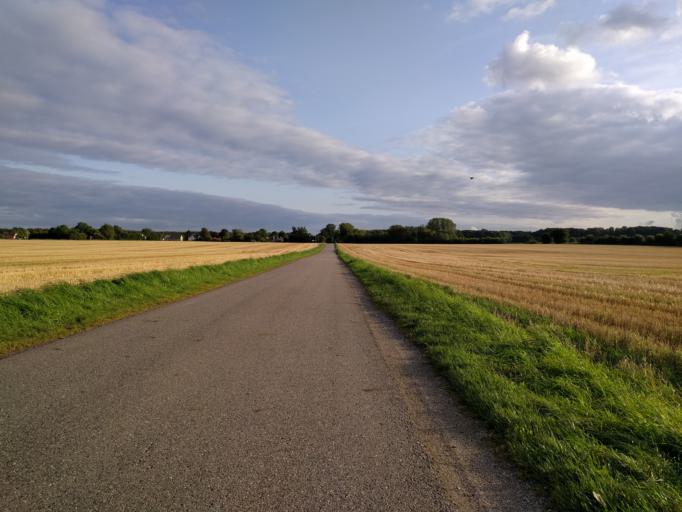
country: DK
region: South Denmark
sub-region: Kerteminde Kommune
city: Kerteminde
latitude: 55.4366
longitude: 10.6152
